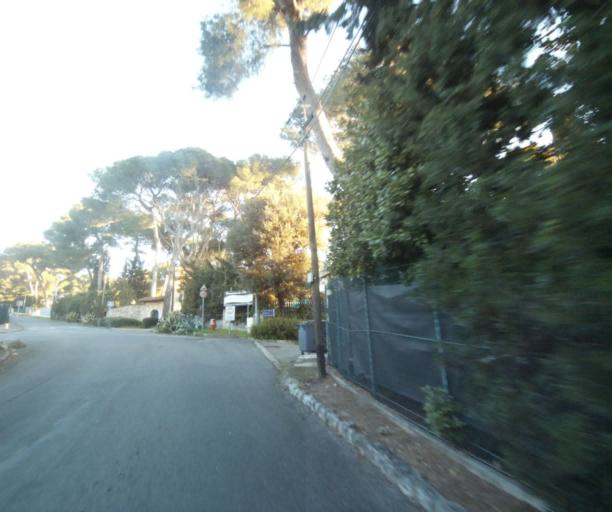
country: FR
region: Provence-Alpes-Cote d'Azur
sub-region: Departement des Alpes-Maritimes
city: Vallauris
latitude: 43.5810
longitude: 7.0848
